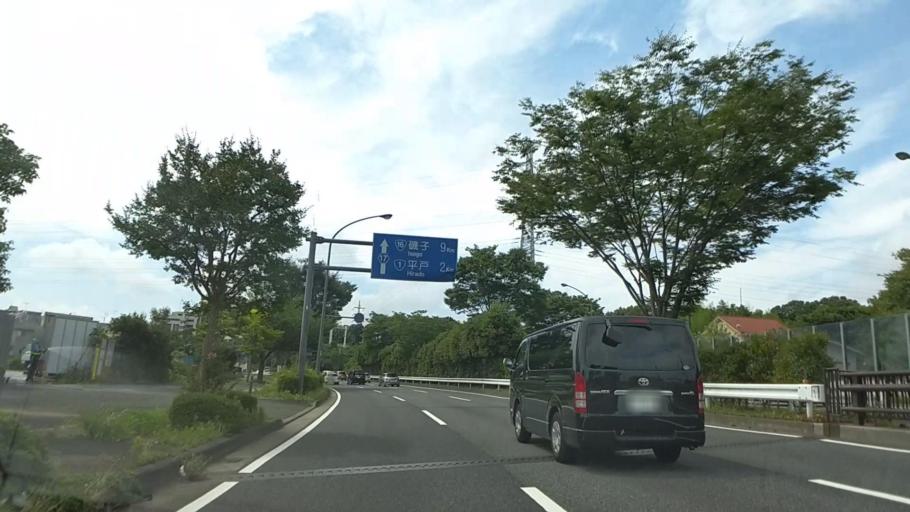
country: JP
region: Kanagawa
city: Yokohama
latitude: 35.4389
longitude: 139.5604
